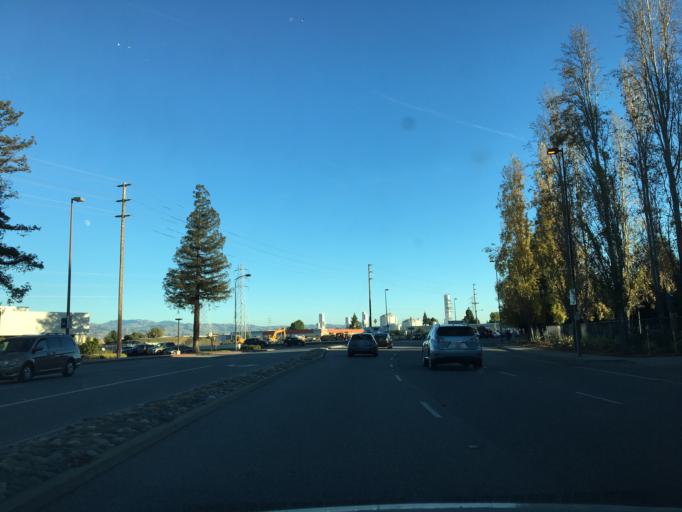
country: US
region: California
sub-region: Santa Clara County
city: Santa Clara
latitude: 37.3884
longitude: -121.9624
